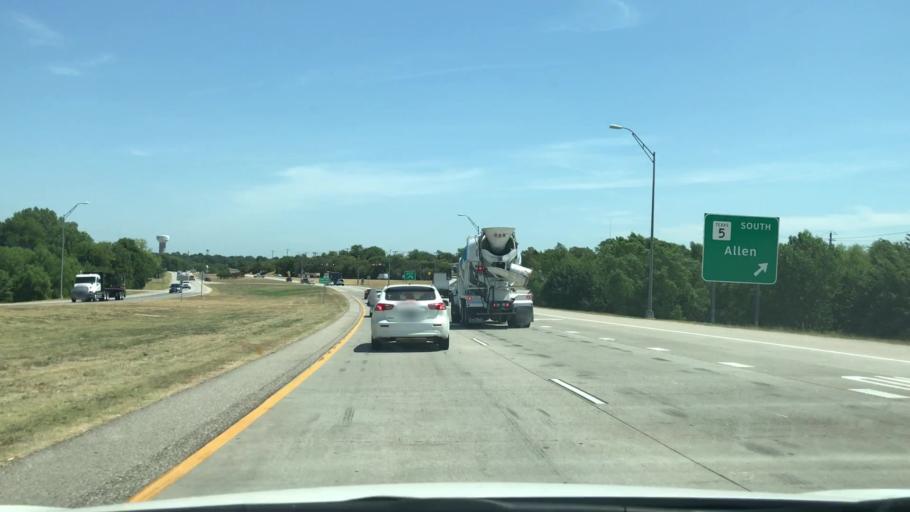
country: US
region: Texas
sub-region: Collin County
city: Fairview
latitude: 33.1648
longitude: -96.6319
